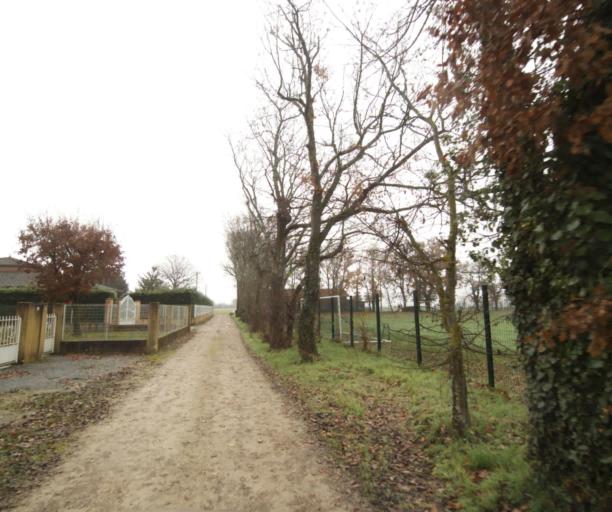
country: FR
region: Midi-Pyrenees
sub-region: Departement de la Haute-Garonne
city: Villemur-sur-Tarn
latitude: 43.8541
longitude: 1.5013
